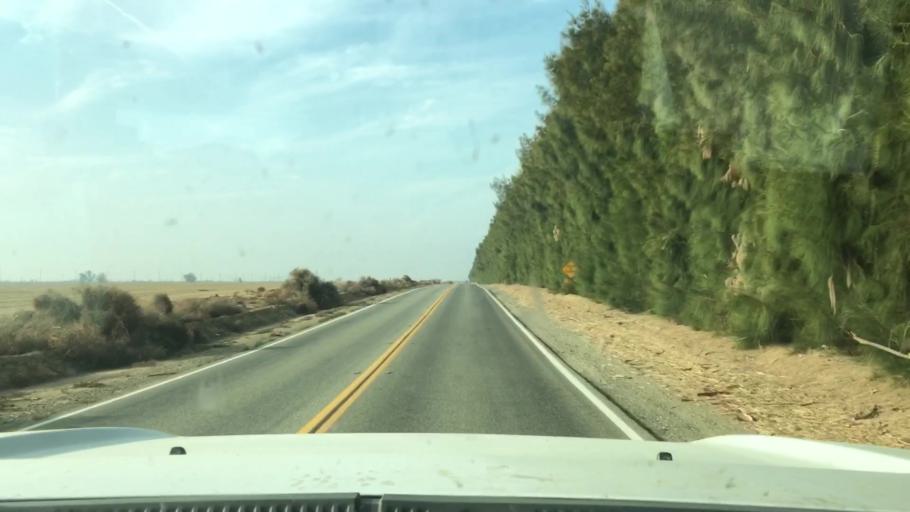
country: US
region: California
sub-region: Kern County
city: Lost Hills
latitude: 35.5015
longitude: -119.7413
